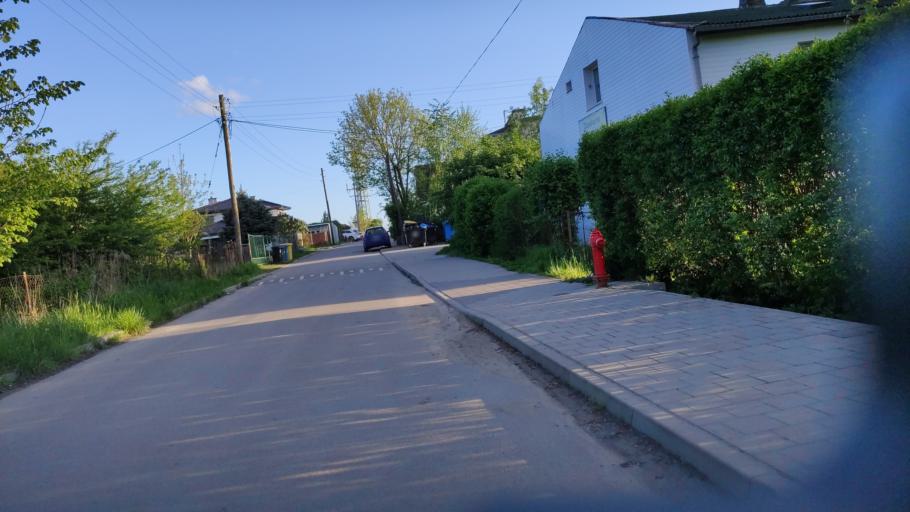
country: PL
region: Lower Silesian Voivodeship
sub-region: Powiat wroclawski
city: Zerniki Wroclawskie
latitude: 51.0472
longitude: 17.0526
